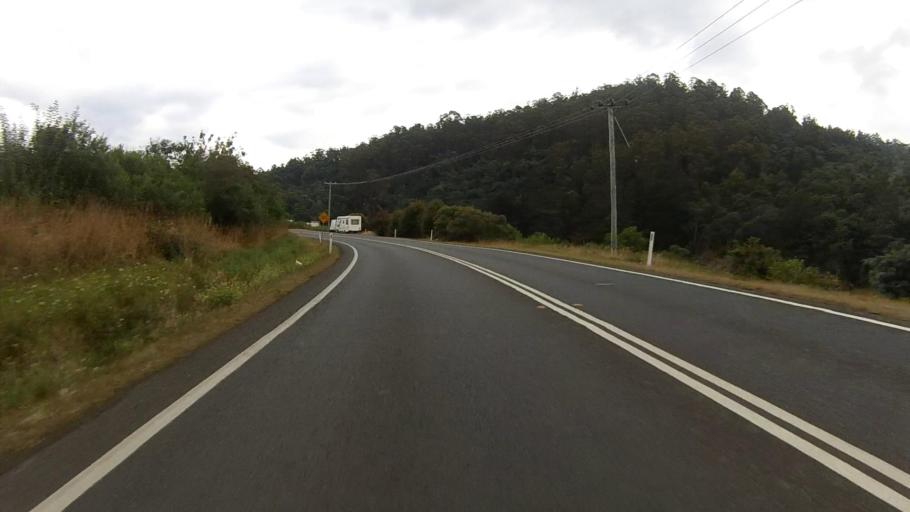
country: AU
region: Tasmania
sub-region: Huon Valley
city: Cygnet
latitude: -43.1419
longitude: 147.0638
